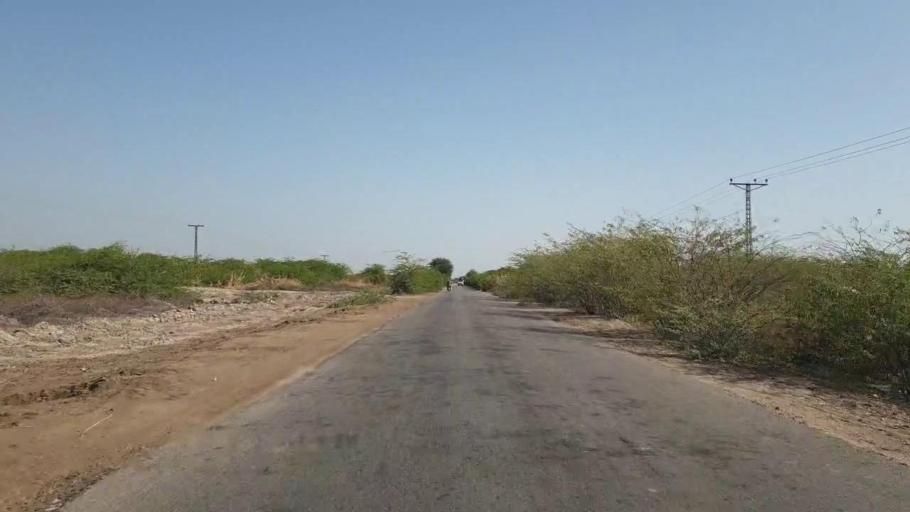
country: PK
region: Sindh
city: Chor
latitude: 25.4705
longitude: 69.7701
